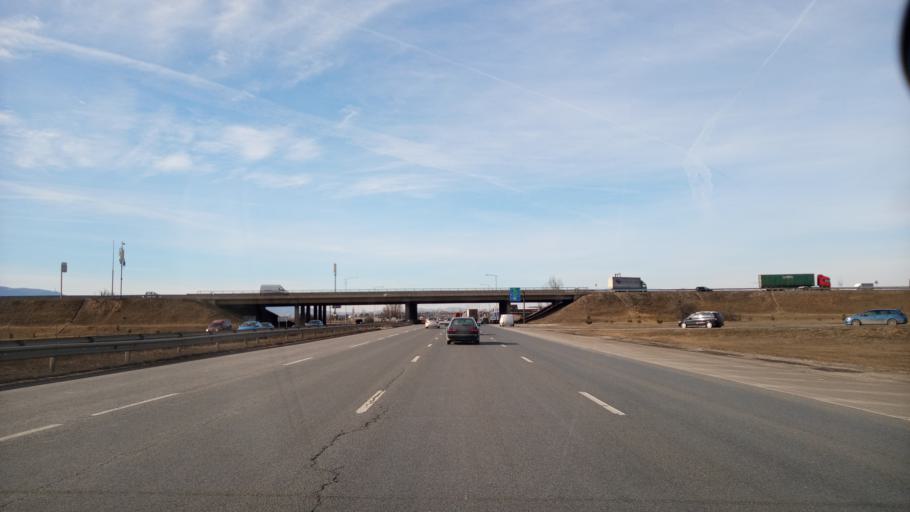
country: BG
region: Sofia-Capital
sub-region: Stolichna Obshtina
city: Sofia
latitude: 42.7077
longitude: 23.4518
